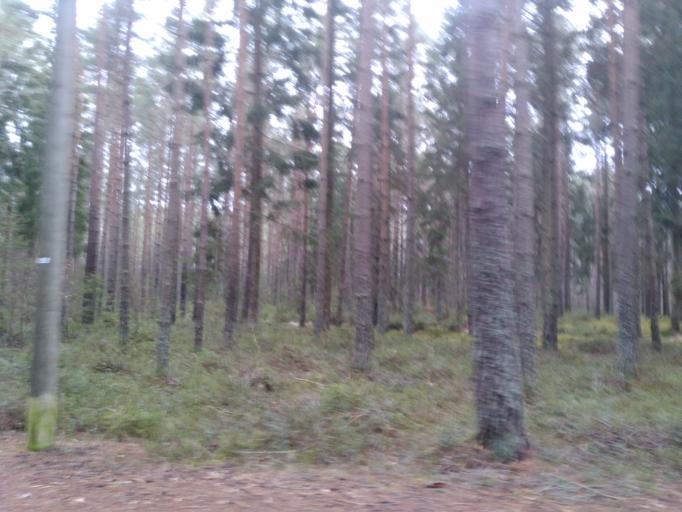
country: SE
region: Vaestra Goetaland
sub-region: Lidkopings Kommun
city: Lidkoping
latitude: 58.4859
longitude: 13.1620
